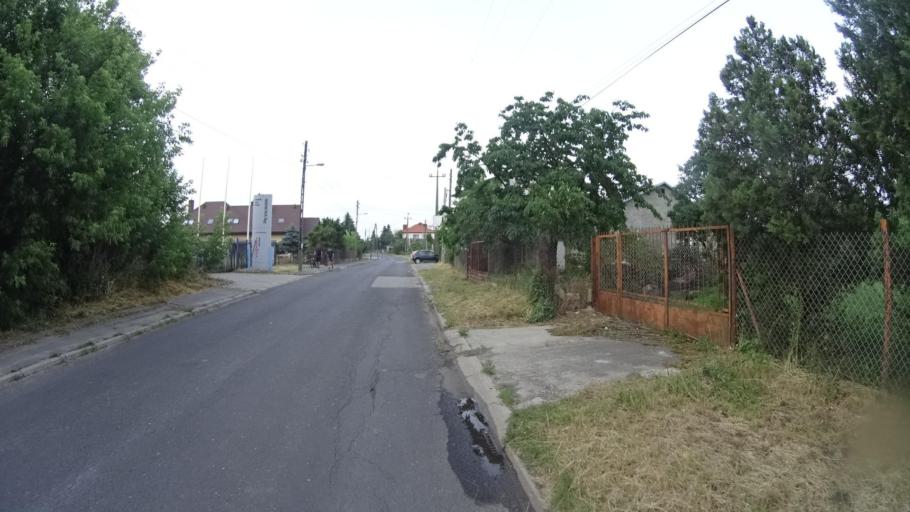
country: PL
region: Masovian Voivodeship
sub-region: Powiat pruszkowski
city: Nowe Grocholice
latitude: 52.1790
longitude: 20.9203
